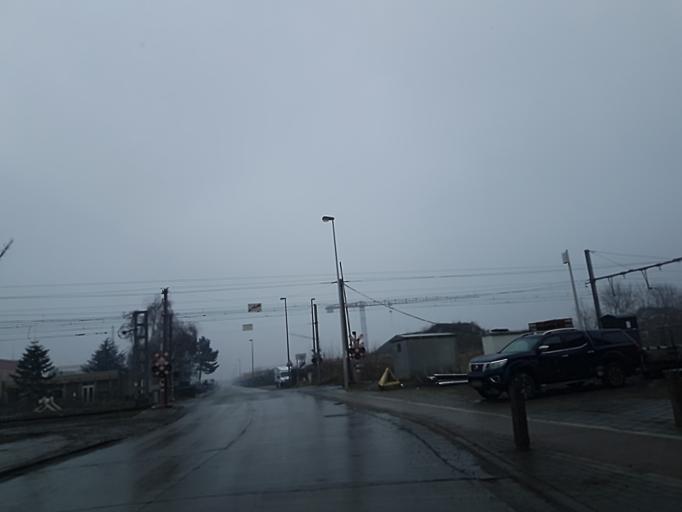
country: BE
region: Flanders
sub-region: Provincie West-Vlaanderen
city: Bredene
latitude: 51.2102
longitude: 2.9778
